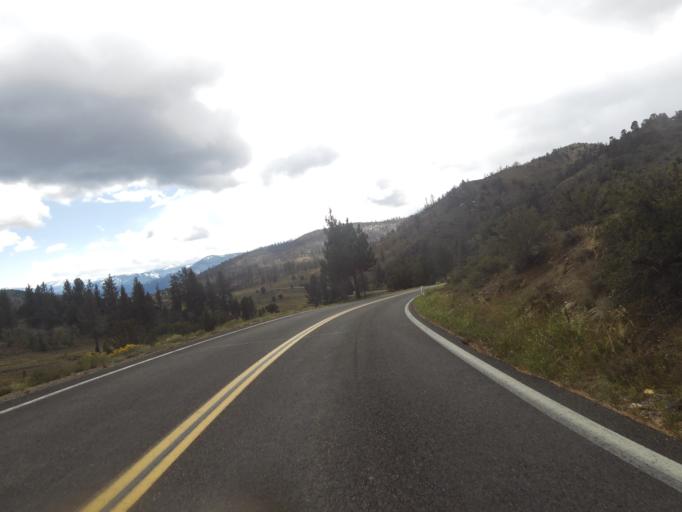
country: US
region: Nevada
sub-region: Douglas County
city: Gardnerville Ranchos
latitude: 38.6700
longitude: -119.6662
